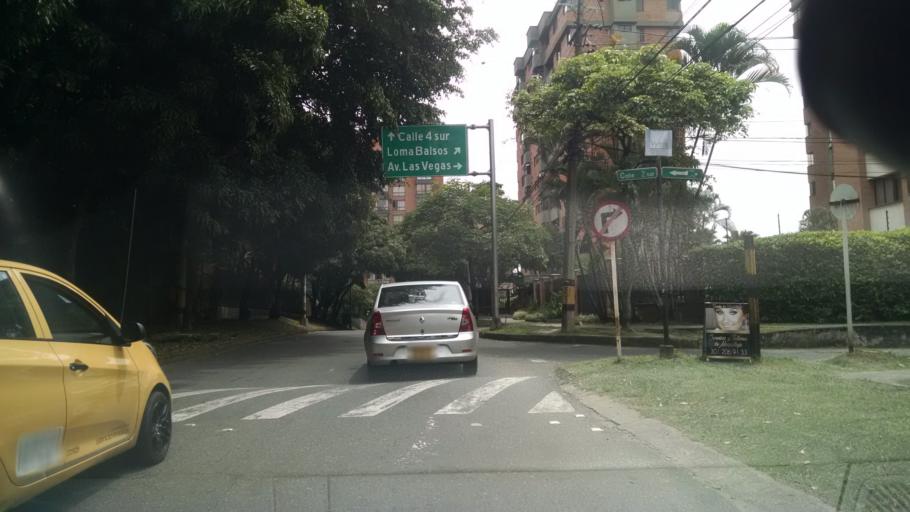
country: CO
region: Antioquia
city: Itagui
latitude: 6.2027
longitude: -75.5742
